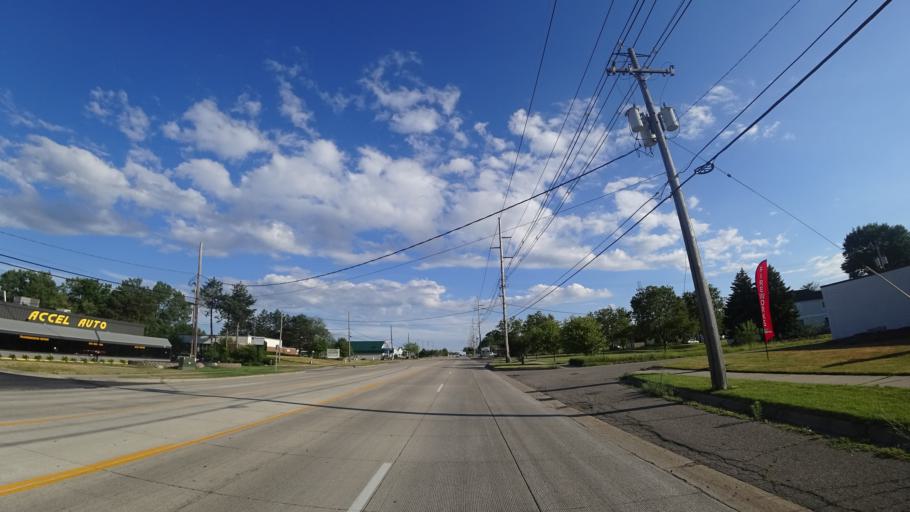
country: US
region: Michigan
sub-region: Ottawa County
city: Holland
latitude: 42.7602
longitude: -86.1166
